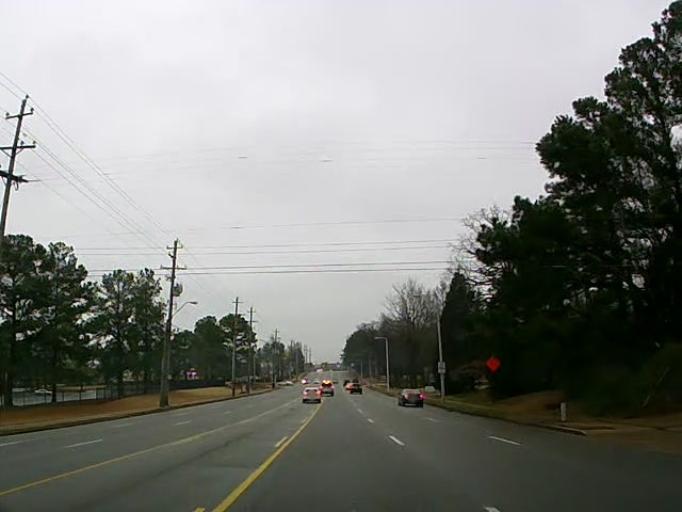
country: US
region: Tennessee
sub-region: Shelby County
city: Germantown
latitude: 35.0940
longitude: -89.8586
